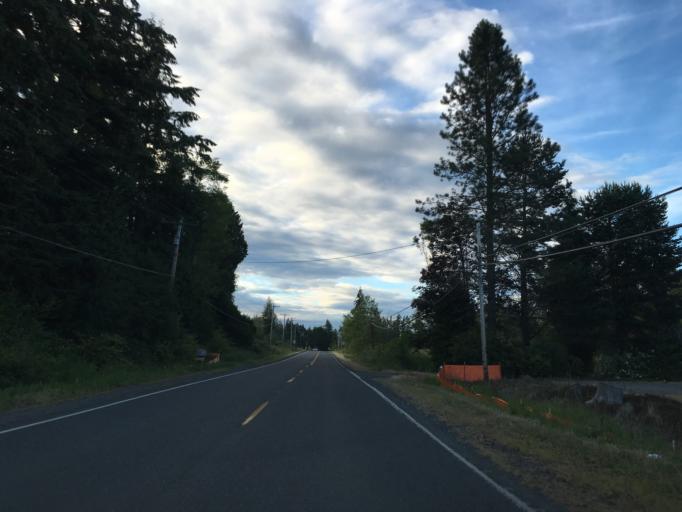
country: US
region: Washington
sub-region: Whatcom County
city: Blaine
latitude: 48.9672
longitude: -122.7300
